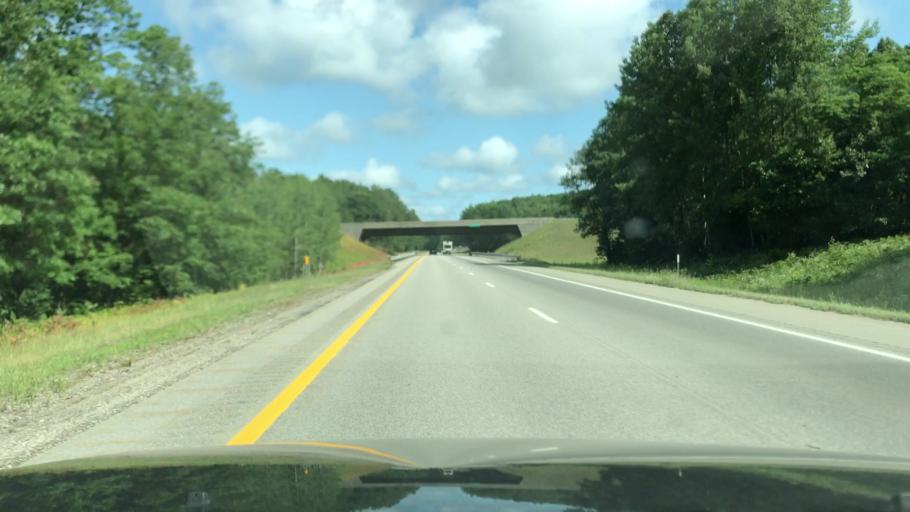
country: US
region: Michigan
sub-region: Montcalm County
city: Howard City
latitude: 43.4880
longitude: -85.4832
